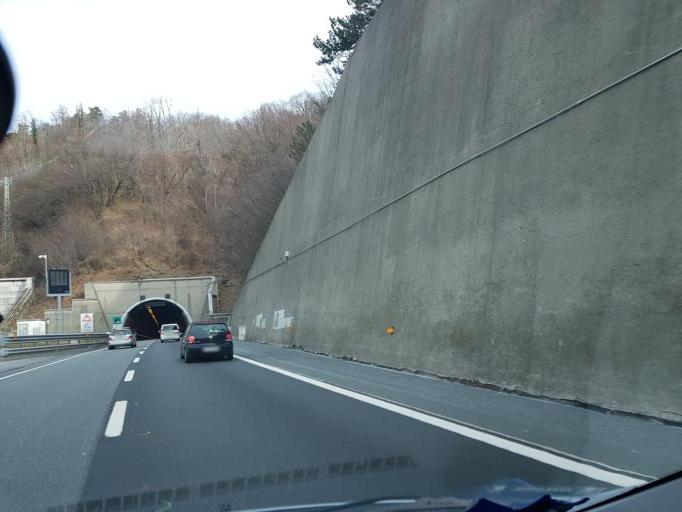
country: IT
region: Liguria
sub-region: Provincia di Genova
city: Busalla
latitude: 44.5503
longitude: 8.9448
